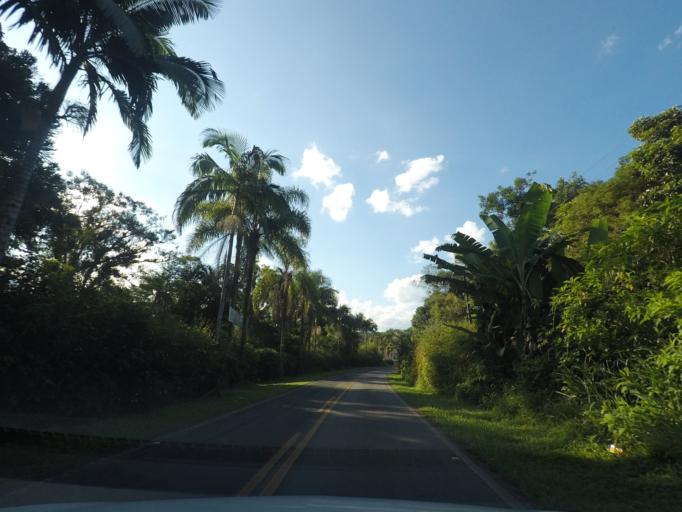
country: BR
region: Parana
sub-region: Antonina
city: Antonina
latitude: -25.4001
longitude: -48.8723
